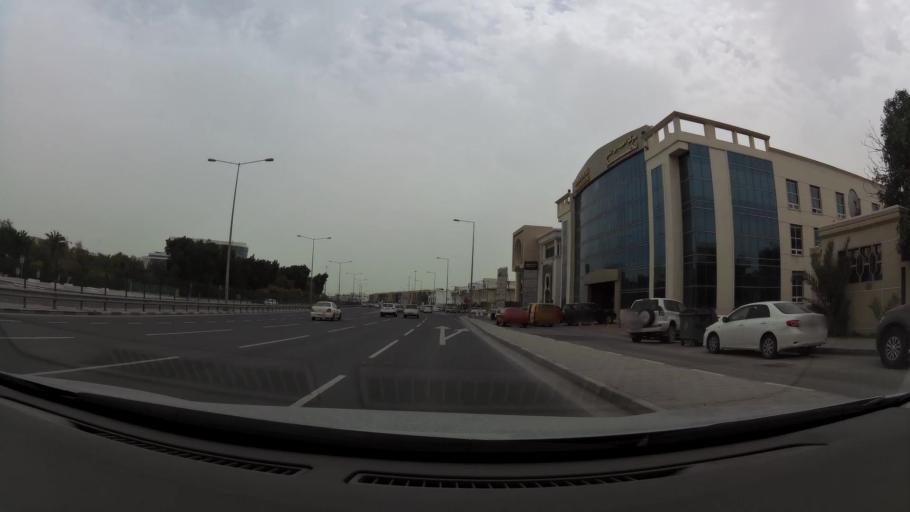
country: QA
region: Baladiyat ad Dawhah
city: Doha
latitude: 25.2638
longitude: 51.5212
